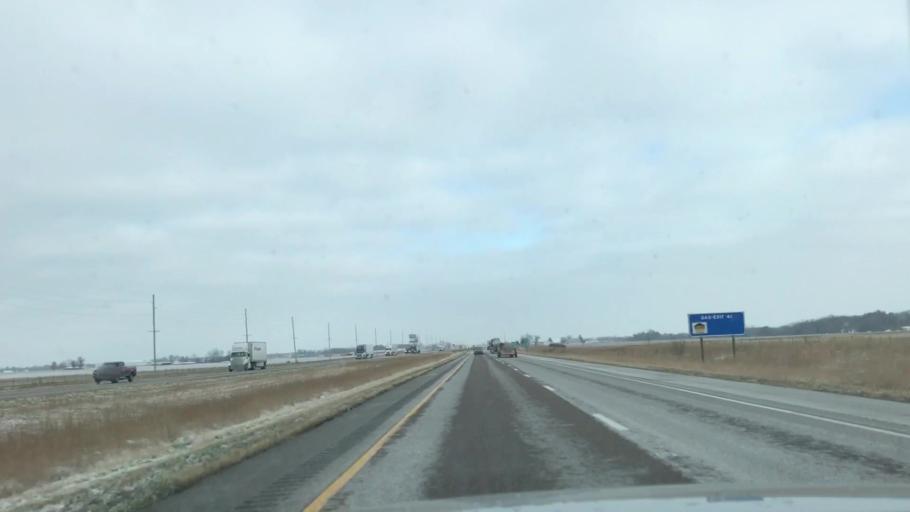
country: US
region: Illinois
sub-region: Macoupin County
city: Staunton
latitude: 38.9957
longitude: -89.7497
